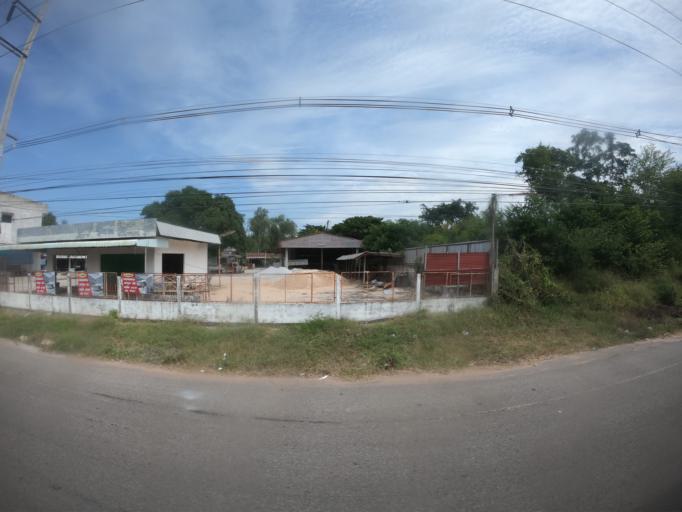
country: TH
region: Maha Sarakham
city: Chiang Yuen
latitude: 16.4149
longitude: 103.0853
